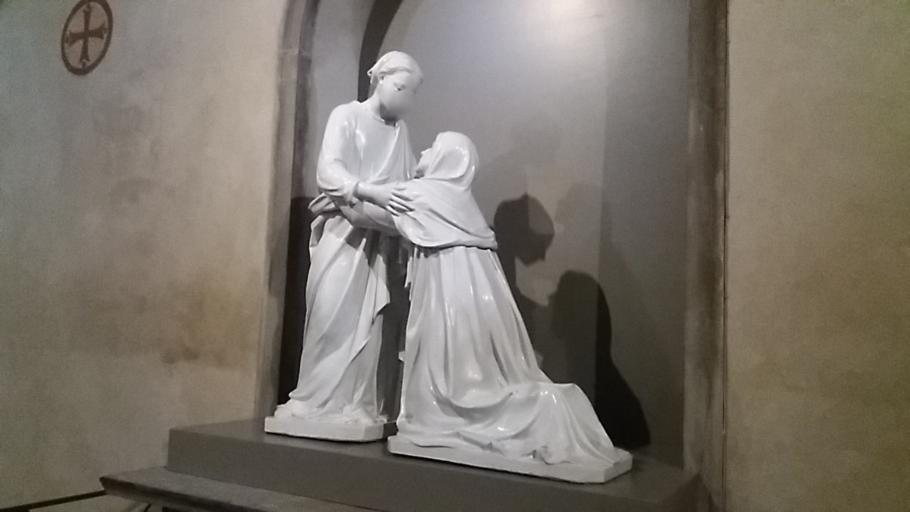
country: IT
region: Tuscany
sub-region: Provincia di Pistoia
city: Pistoia
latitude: 43.9320
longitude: 10.9167
